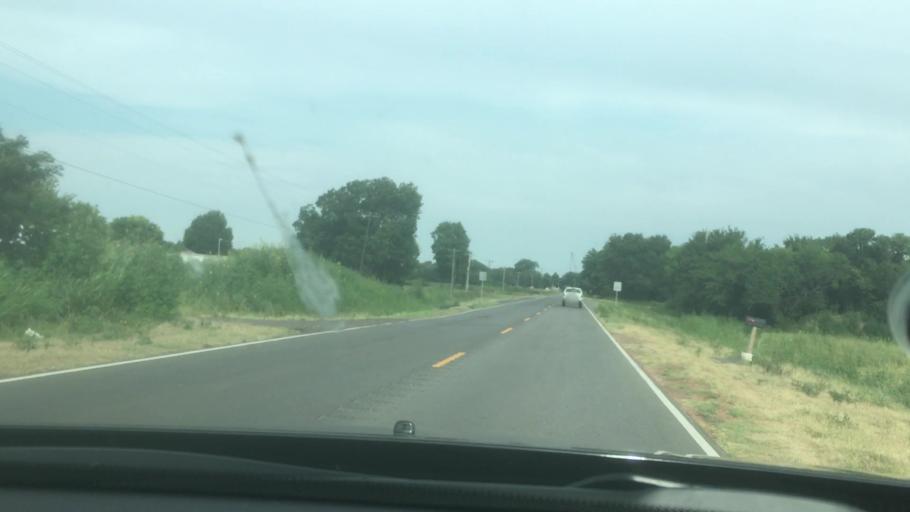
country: US
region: Oklahoma
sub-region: Garvin County
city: Maysville
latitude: 34.8155
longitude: -97.3942
